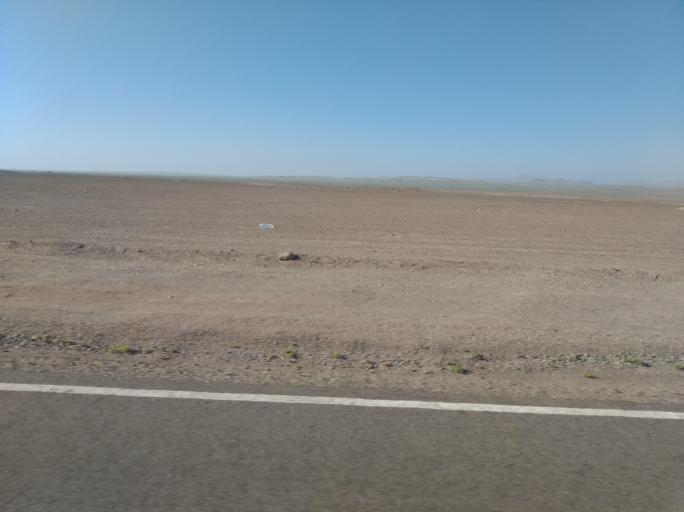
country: CL
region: Atacama
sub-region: Provincia de Copiapo
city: Copiapo
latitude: -27.3193
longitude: -70.8251
